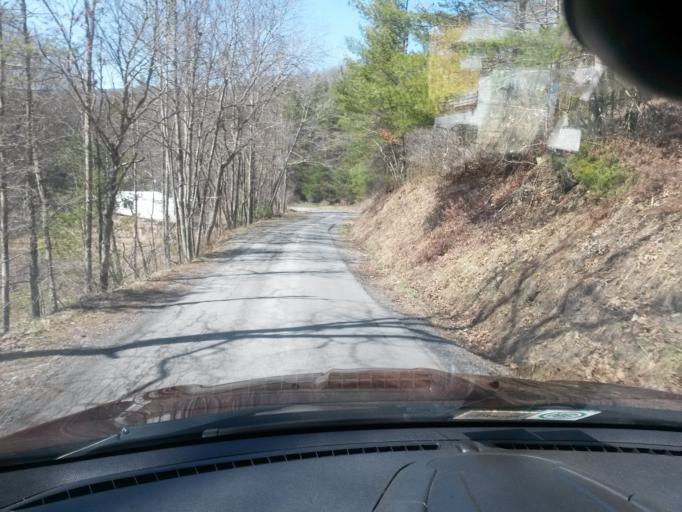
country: US
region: West Virginia
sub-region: Greenbrier County
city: White Sulphur Springs
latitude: 37.6805
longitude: -80.3333
